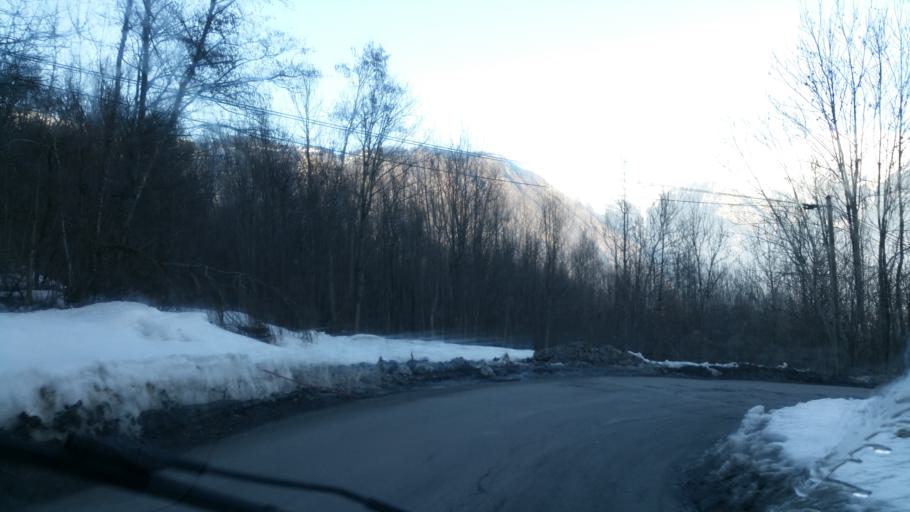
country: FR
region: Rhone-Alpes
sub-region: Departement de la Savoie
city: Saint-Jean-de-Maurienne
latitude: 45.2676
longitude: 6.3122
